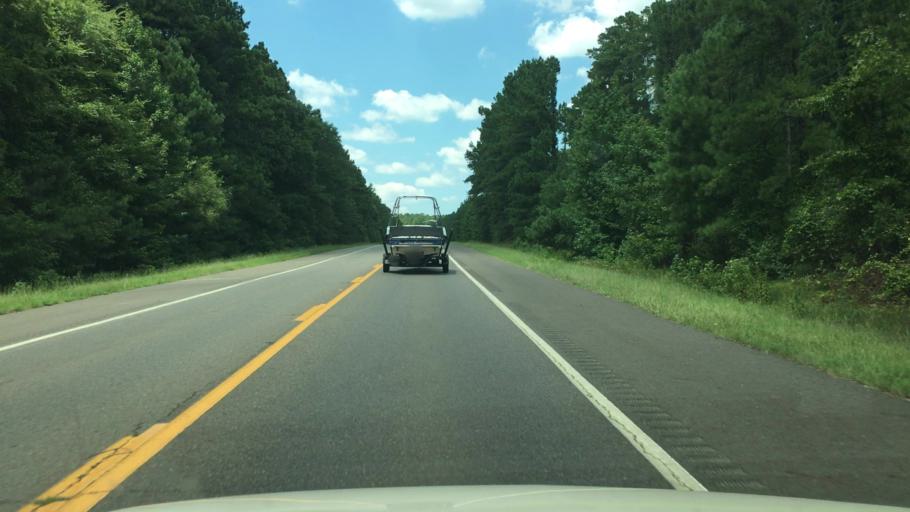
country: US
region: Arkansas
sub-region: Clark County
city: Arkadelphia
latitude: 34.2025
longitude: -93.0782
